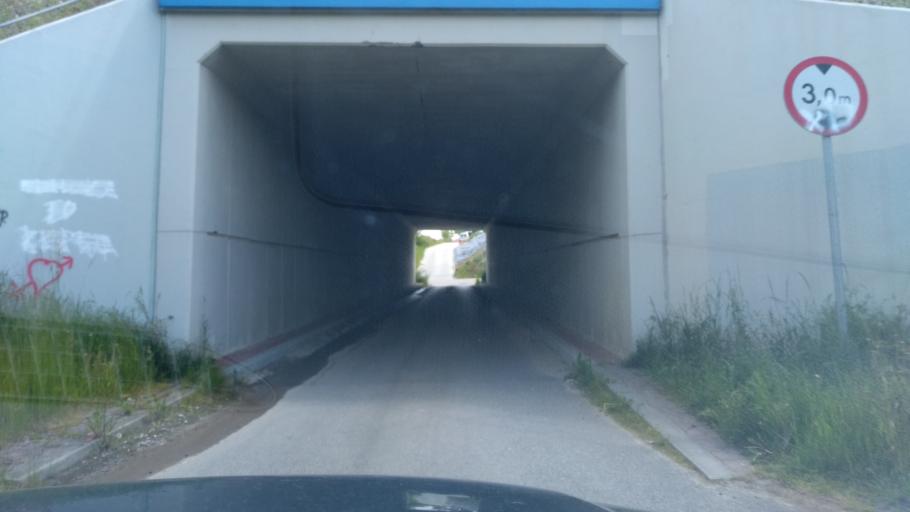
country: PL
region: Subcarpathian Voivodeship
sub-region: Powiat ropczycko-sedziszowski
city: Ropczyce
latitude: 50.0503
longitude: 21.6180
